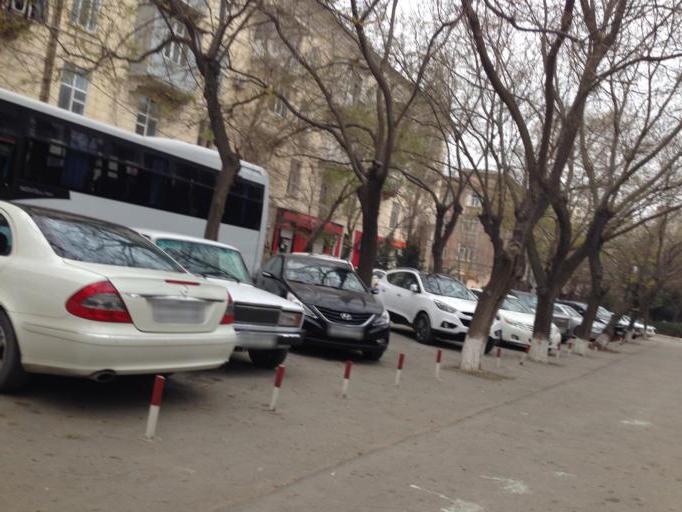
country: AZ
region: Baki
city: Baku
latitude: 40.4010
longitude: 49.8722
